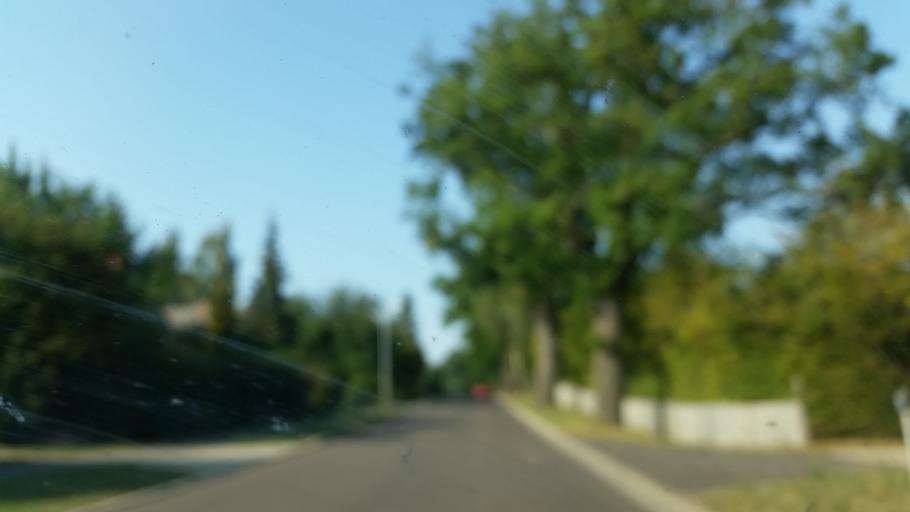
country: DE
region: Brandenburg
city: Pinnow
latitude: 53.0198
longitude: 14.0824
